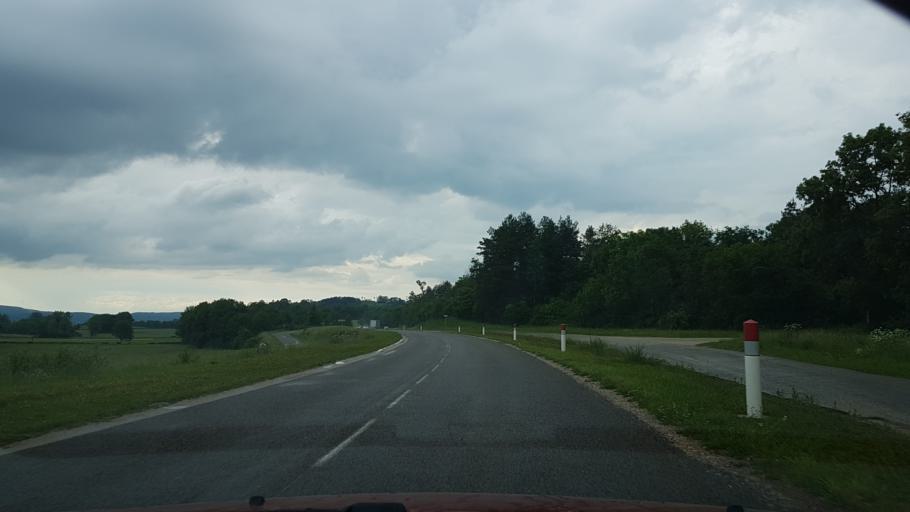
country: FR
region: Franche-Comte
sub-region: Departement du Jura
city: Clairvaux-les-Lacs
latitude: 46.5536
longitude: 5.7454
